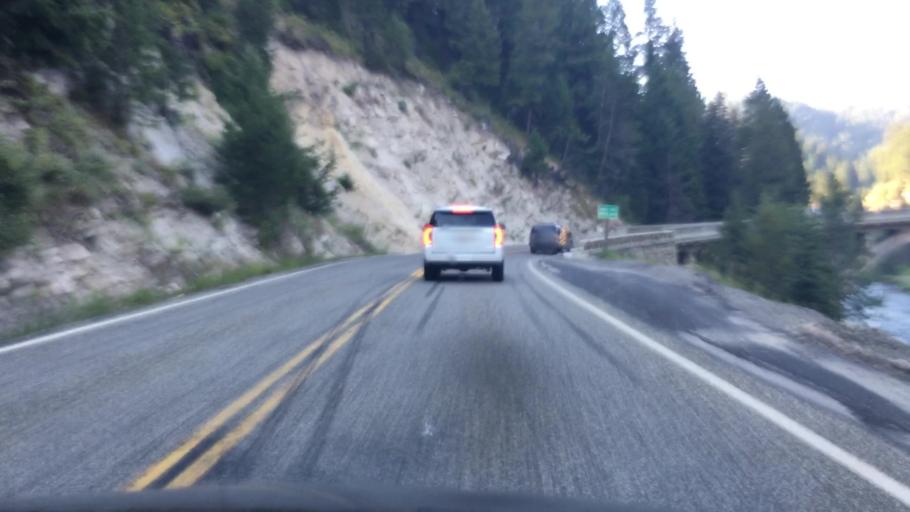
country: US
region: Idaho
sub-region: Valley County
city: Cascade
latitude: 44.3241
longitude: -116.0603
